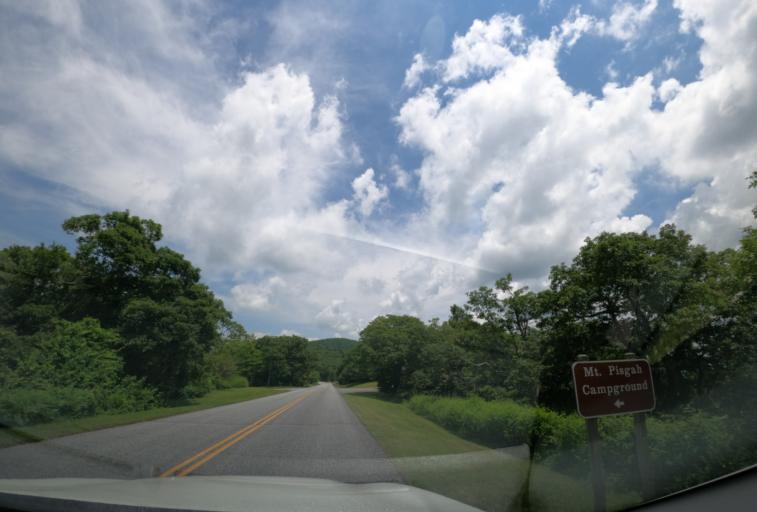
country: US
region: North Carolina
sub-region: Haywood County
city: Canton
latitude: 35.4022
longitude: -82.7569
